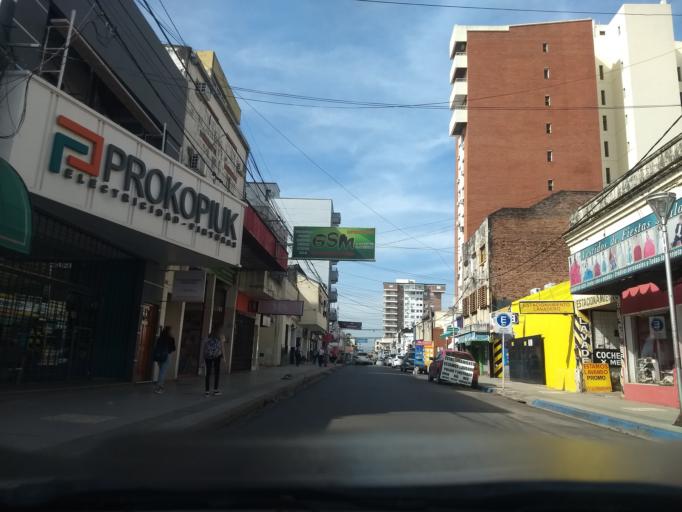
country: AR
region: Corrientes
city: Corrientes
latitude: -27.4695
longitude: -58.8277
